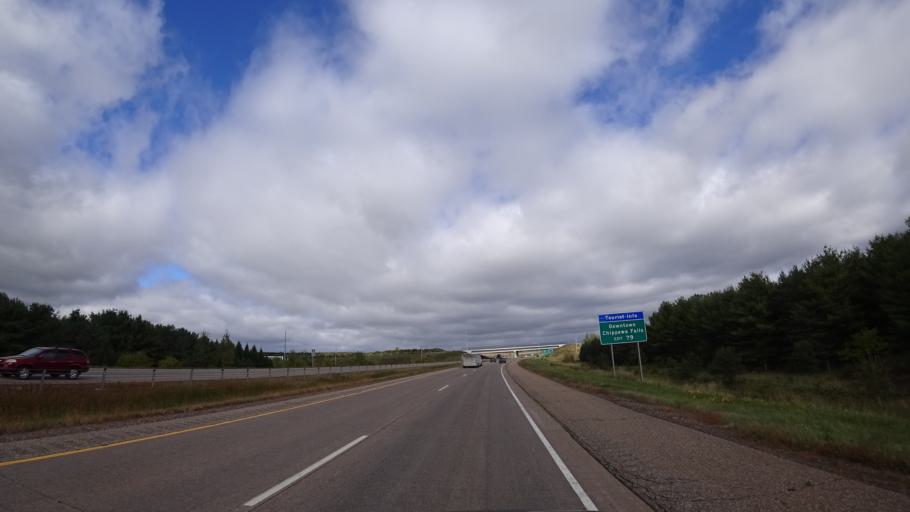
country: US
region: Wisconsin
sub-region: Chippewa County
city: Chippewa Falls
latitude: 44.9127
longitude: -91.3716
